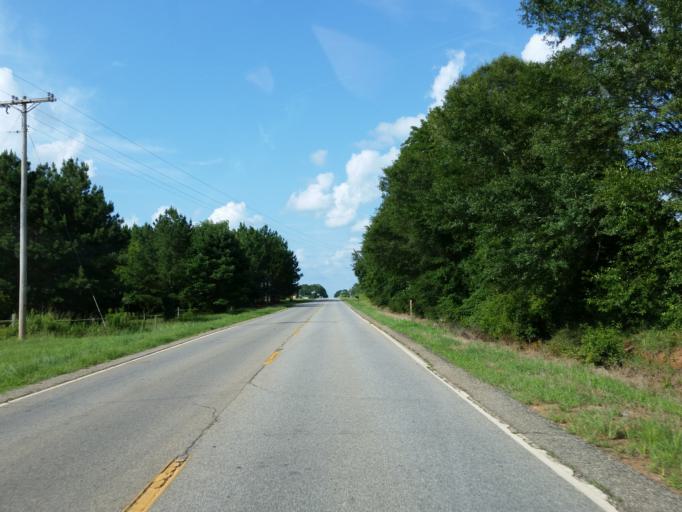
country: US
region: Georgia
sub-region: Lee County
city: Leesburg
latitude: 31.8166
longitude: -84.1121
